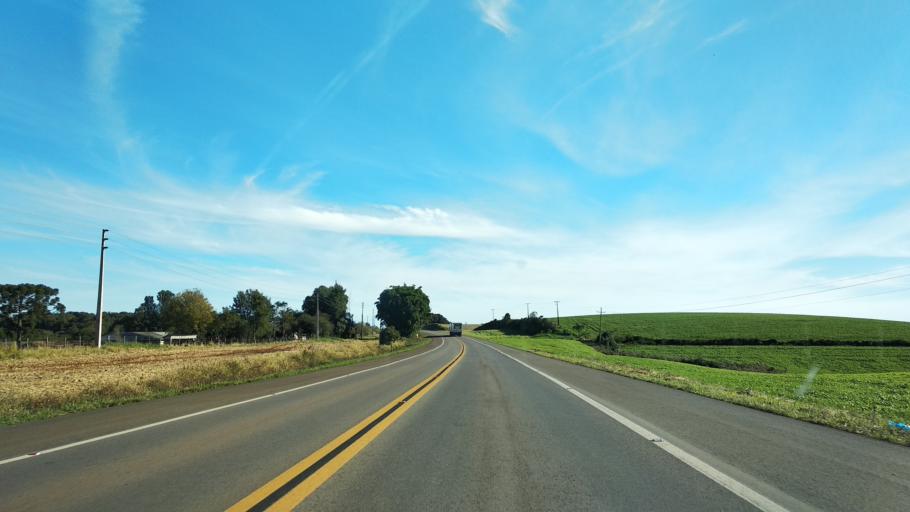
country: BR
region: Santa Catarina
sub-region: Celso Ramos
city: Celso Ramos
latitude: -27.4930
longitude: -51.3348
